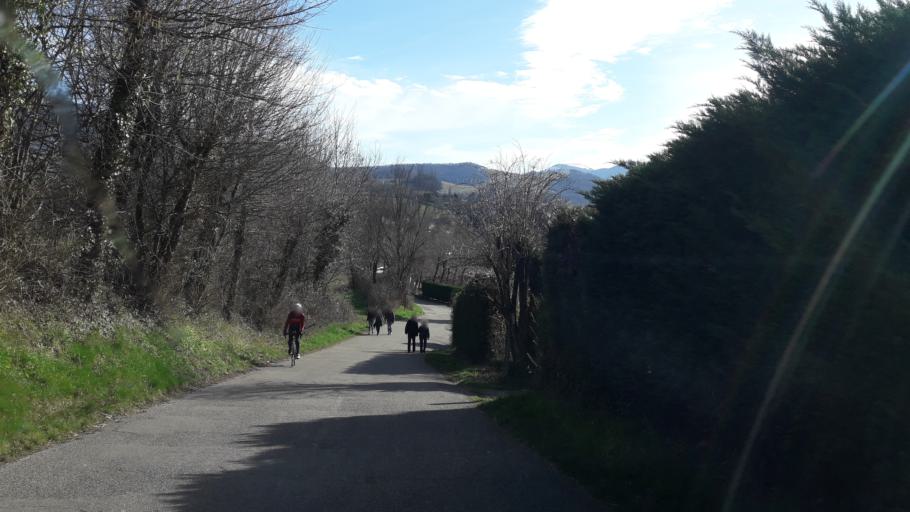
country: FR
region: Rhone-Alpes
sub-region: Departement de l'Isere
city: Brie-et-Angonnes
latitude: 45.1369
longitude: 5.7784
